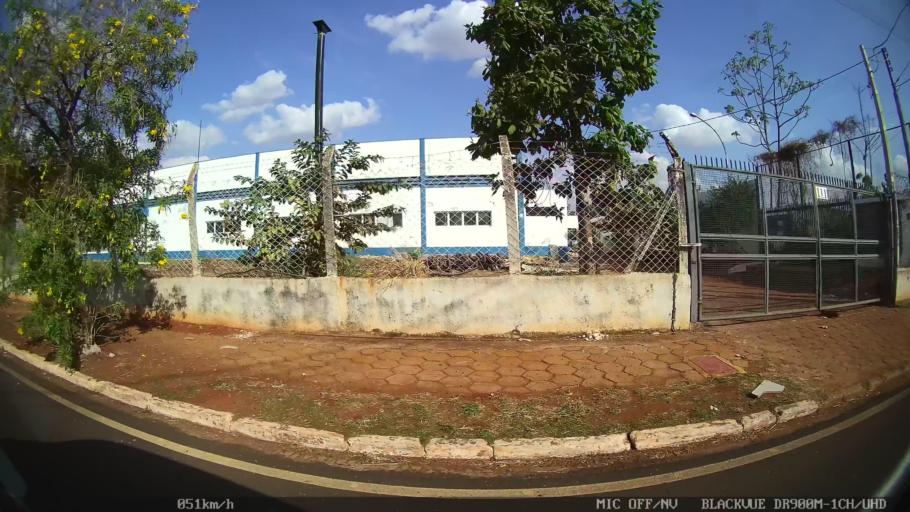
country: BR
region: Sao Paulo
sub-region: Ribeirao Preto
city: Ribeirao Preto
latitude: -21.1783
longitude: -47.8244
